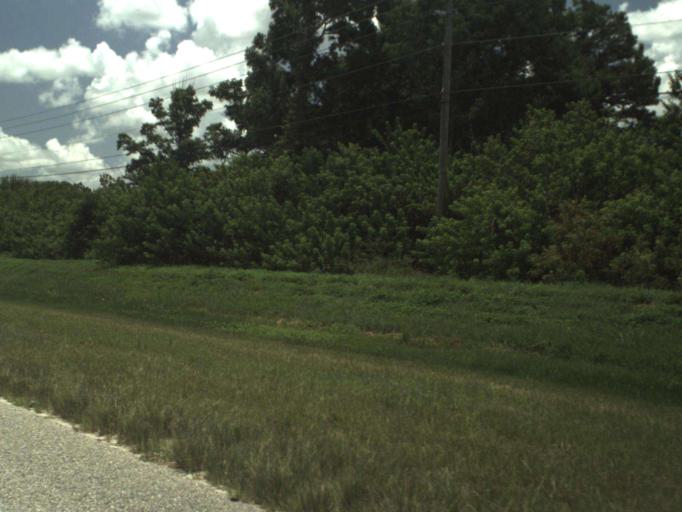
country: US
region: Florida
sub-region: Indian River County
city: Fellsmere
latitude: 27.6403
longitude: -80.6511
